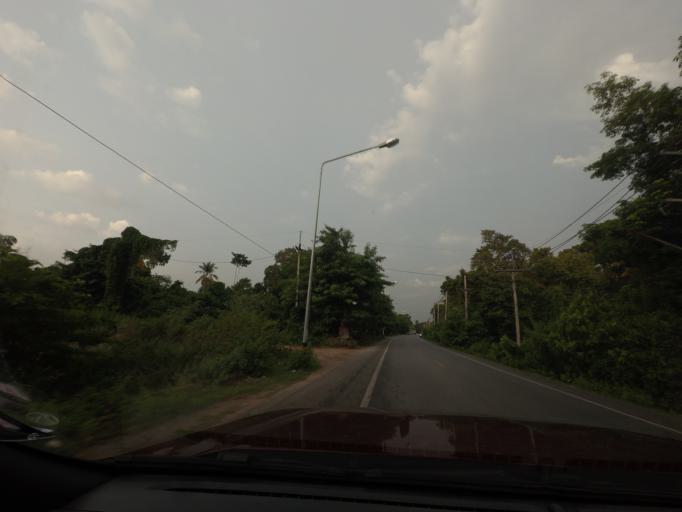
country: TH
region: Yala
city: Yala
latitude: 6.5479
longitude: 101.2453
